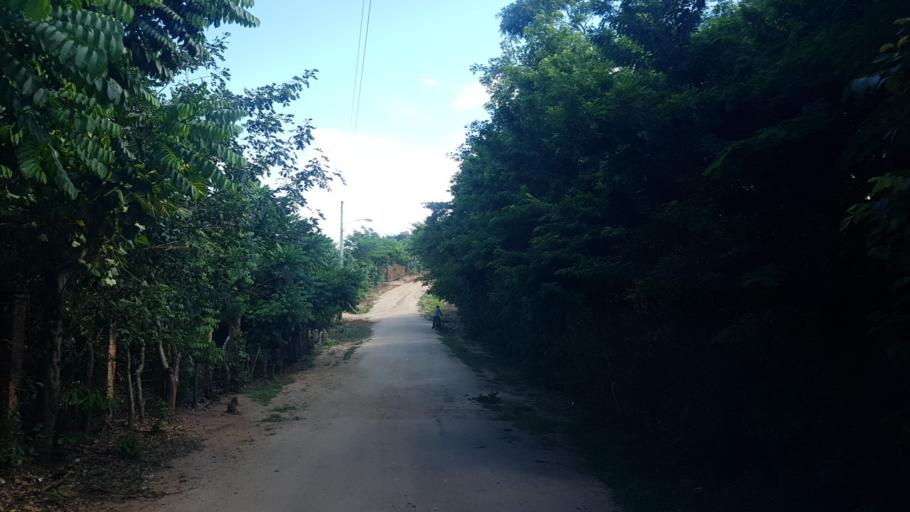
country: NI
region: Nueva Segovia
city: Mozonte
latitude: 13.6527
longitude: -86.3982
